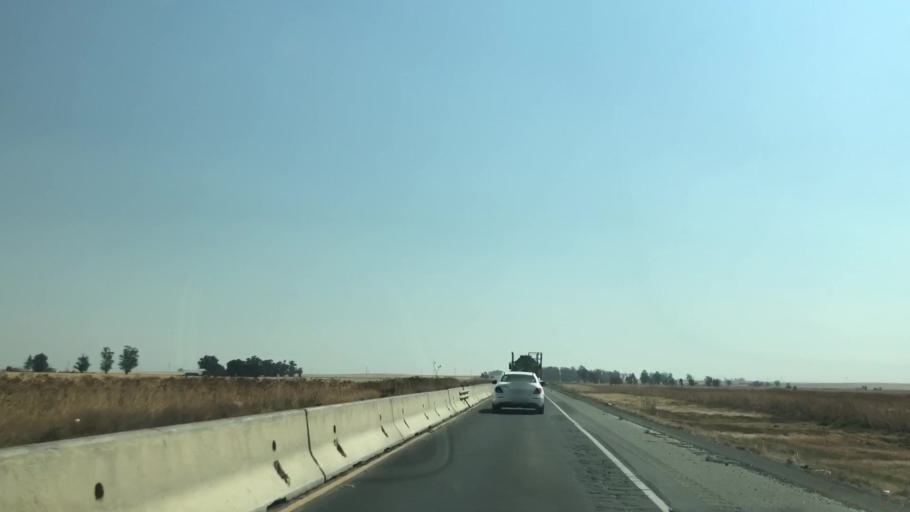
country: US
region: California
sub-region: Solano County
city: Suisun
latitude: 38.2284
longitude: -121.9186
